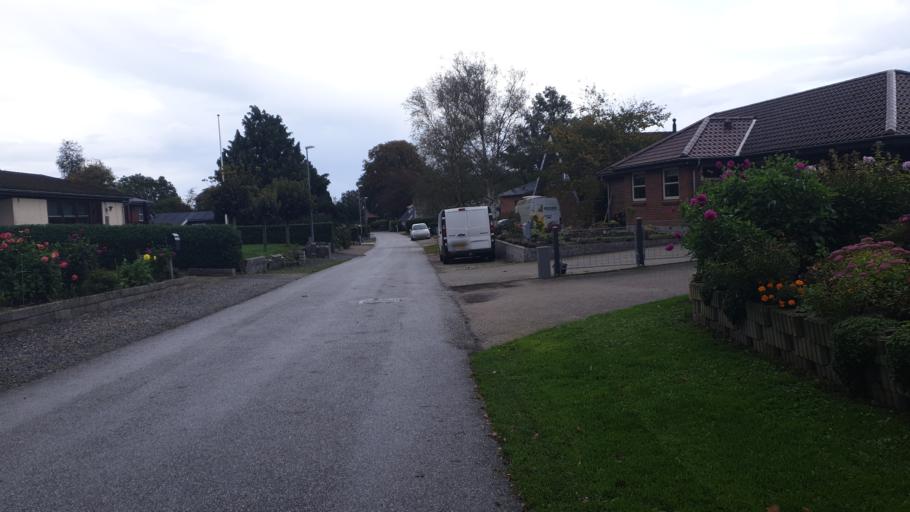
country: DK
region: Central Jutland
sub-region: Hedensted Kommune
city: Hedensted
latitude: 55.8046
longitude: 9.7055
